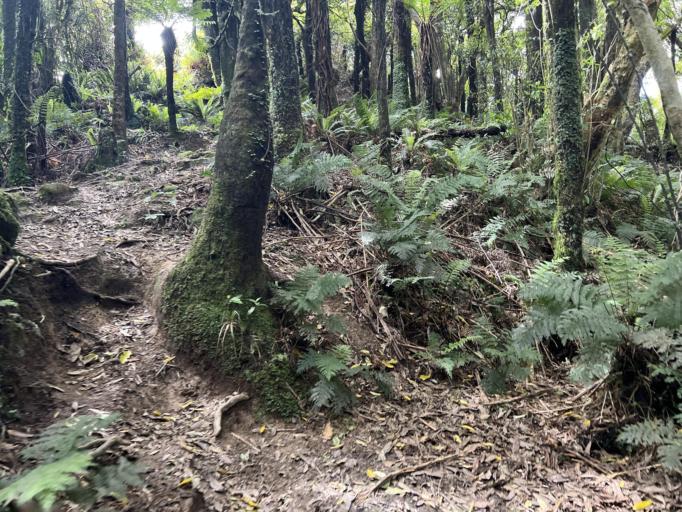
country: NZ
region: Wellington
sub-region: Kapiti Coast District
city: Paraparaumu
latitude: -40.8781
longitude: 175.0912
